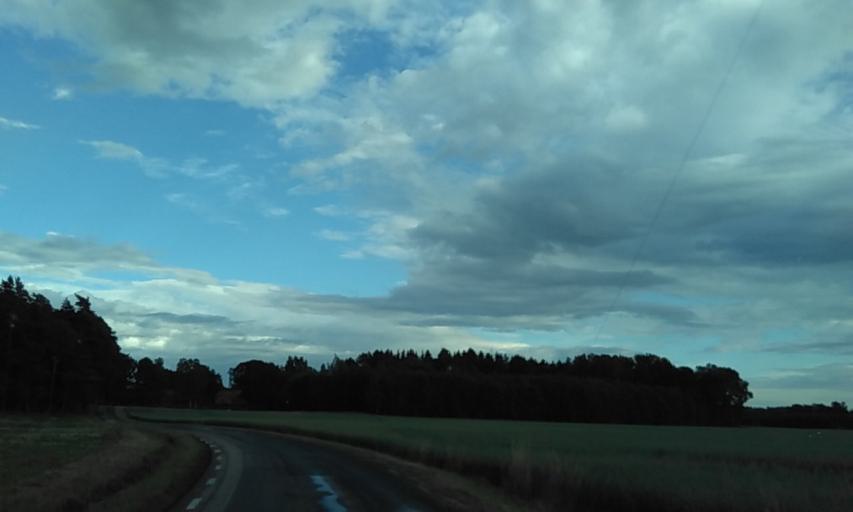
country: SE
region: Vaestra Goetaland
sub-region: Grastorps Kommun
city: Graestorp
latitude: 58.3841
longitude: 12.7555
